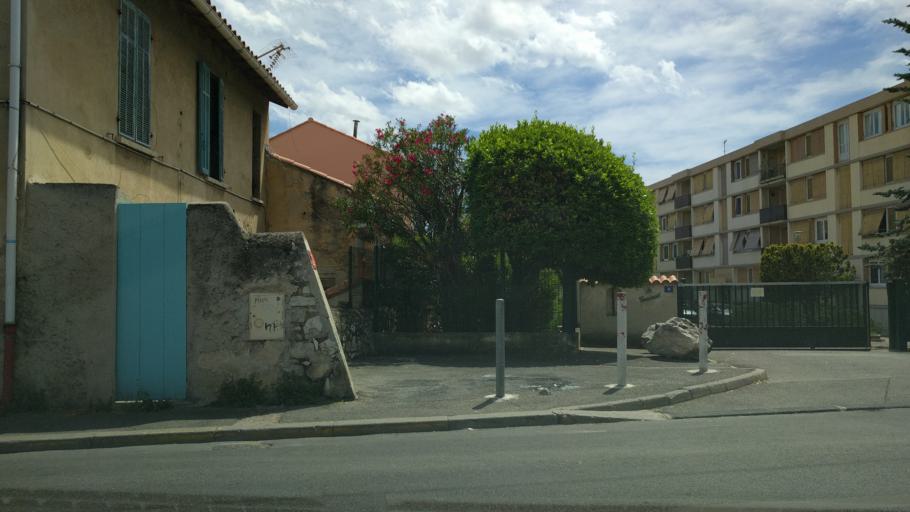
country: FR
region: Provence-Alpes-Cote d'Azur
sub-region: Departement des Bouches-du-Rhone
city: Marseille 13
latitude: 43.3378
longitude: 5.4065
